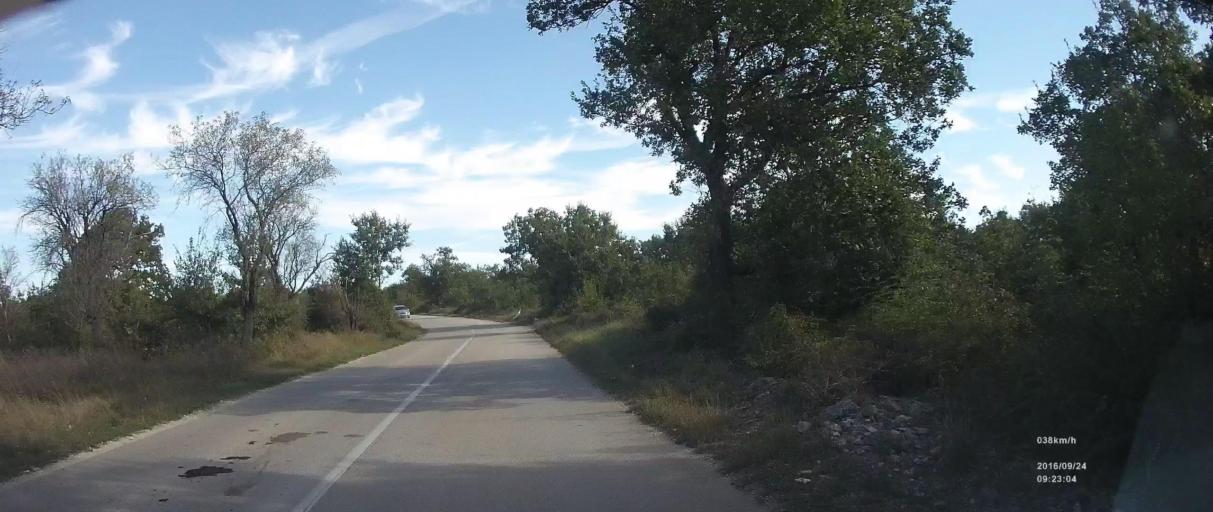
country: HR
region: Zadarska
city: Polaca
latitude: 44.0717
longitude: 15.4748
